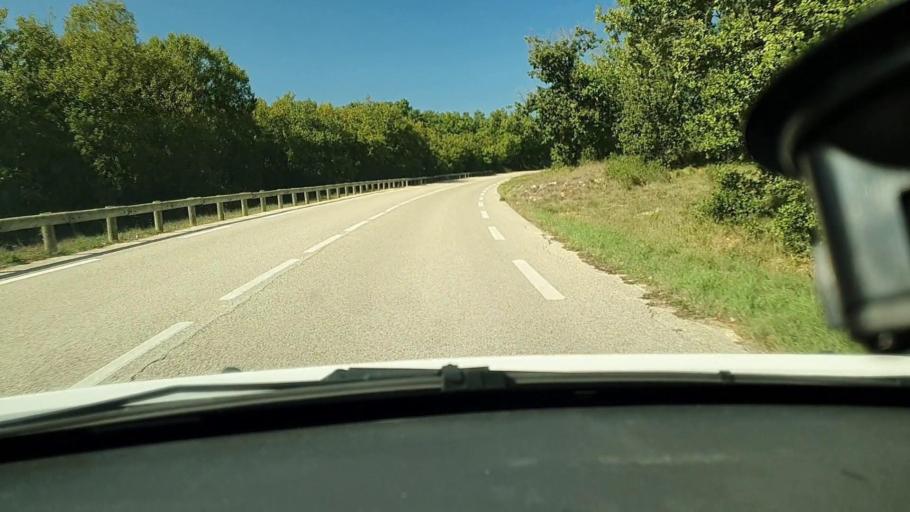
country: FR
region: Languedoc-Roussillon
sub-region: Departement du Gard
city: Barjac
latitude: 44.2174
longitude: 4.3254
